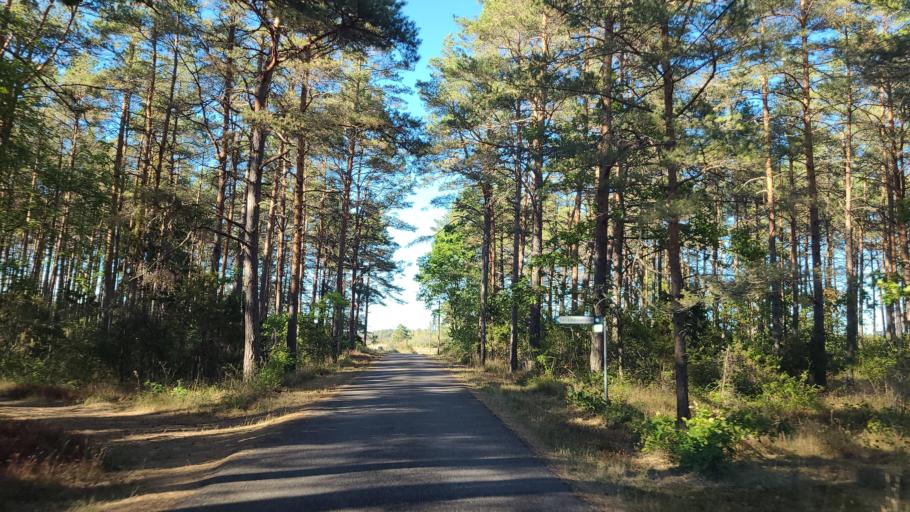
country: SE
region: Kalmar
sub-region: Borgholms Kommun
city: Borgholm
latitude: 57.3159
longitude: 17.0509
